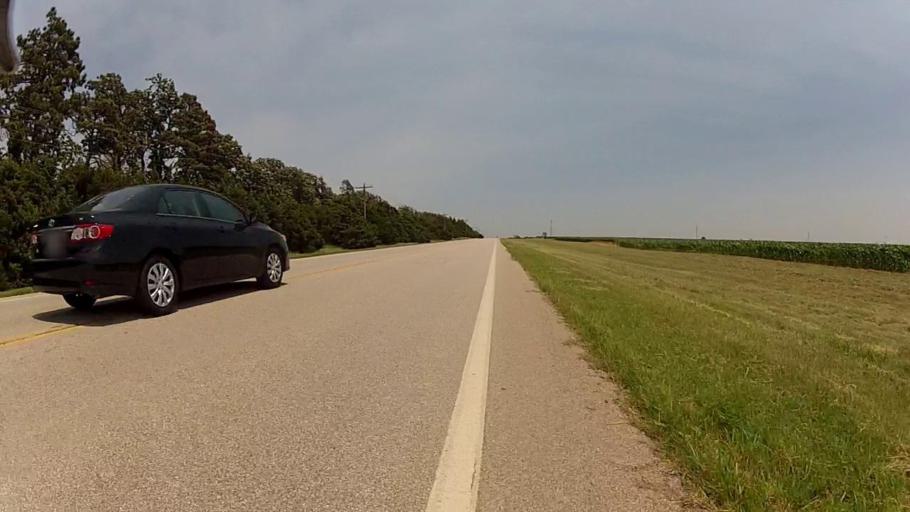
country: US
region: Kansas
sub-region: Cowley County
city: Arkansas City
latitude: 37.0566
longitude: -97.1629
